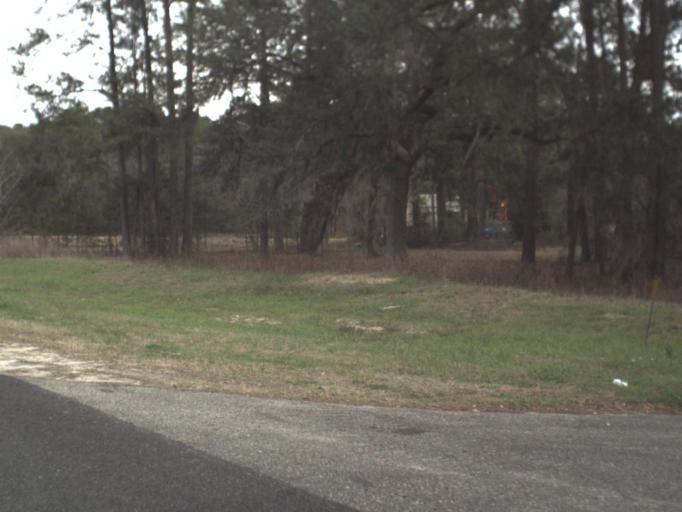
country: US
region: Florida
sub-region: Leon County
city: Tallahassee
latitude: 30.5737
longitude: -84.2050
